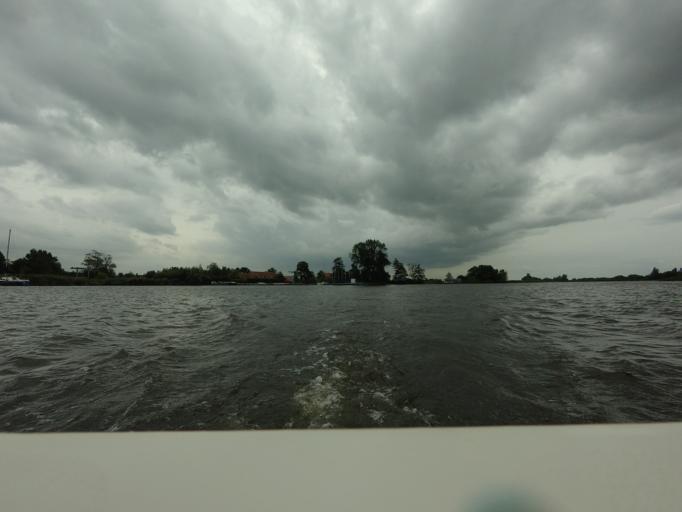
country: NL
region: Friesland
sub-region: Gemeente Smallingerland
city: Oudega
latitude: 53.0984
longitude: 5.9453
